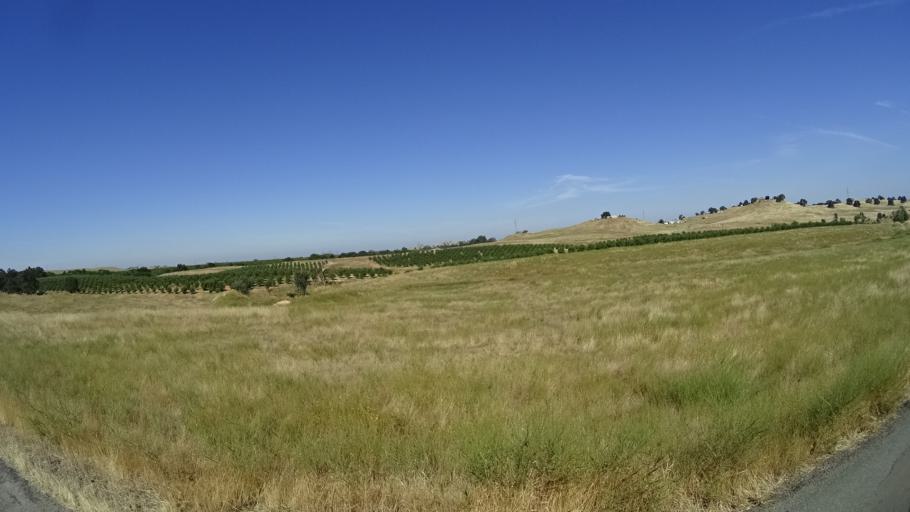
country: US
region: California
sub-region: Calaveras County
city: Rancho Calaveras
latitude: 38.0809
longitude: -120.9108
